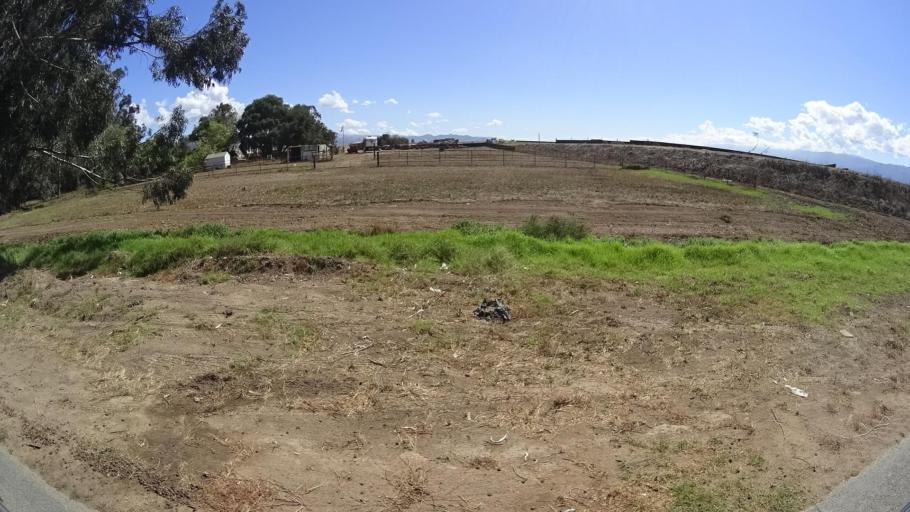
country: US
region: California
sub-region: Monterey County
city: Chualar
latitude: 36.6522
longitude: -121.5615
